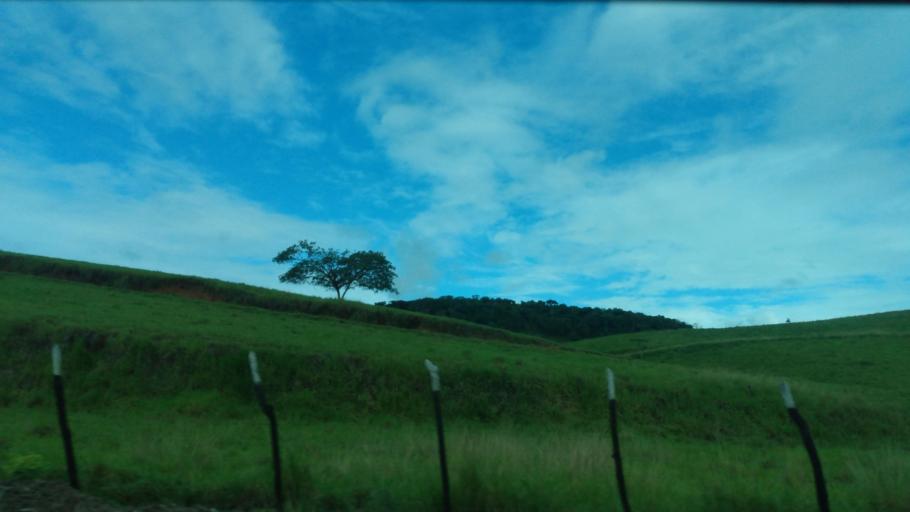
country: BR
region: Pernambuco
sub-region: Catende
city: Catende
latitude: -8.7067
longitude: -35.7601
